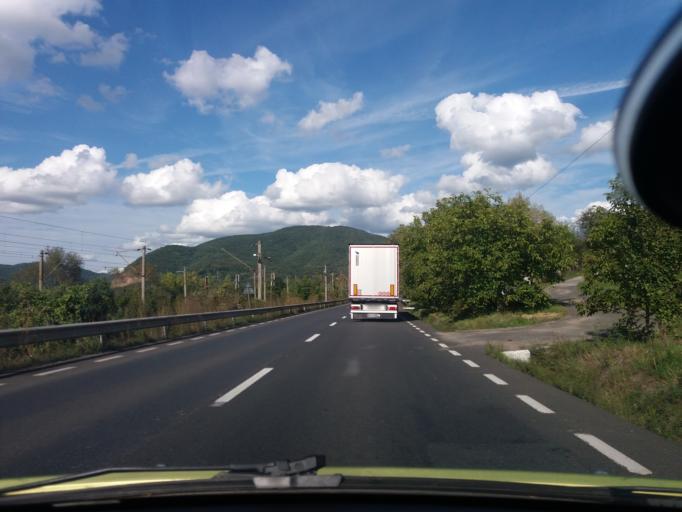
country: RO
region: Hunedoara
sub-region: Comuna Zam
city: Zam
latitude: 45.9943
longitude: 22.4361
